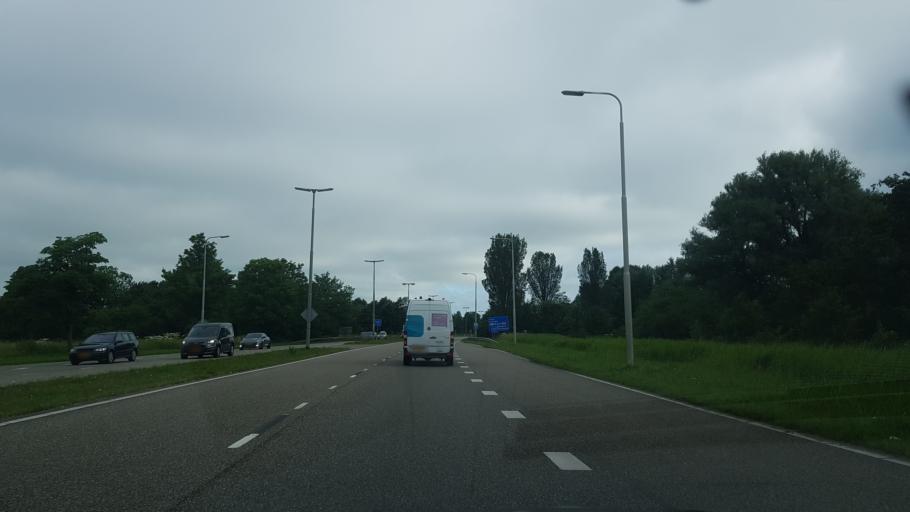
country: NL
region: Friesland
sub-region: Gemeente Leeuwarden
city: Camminghaburen
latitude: 53.2125
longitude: 5.8302
